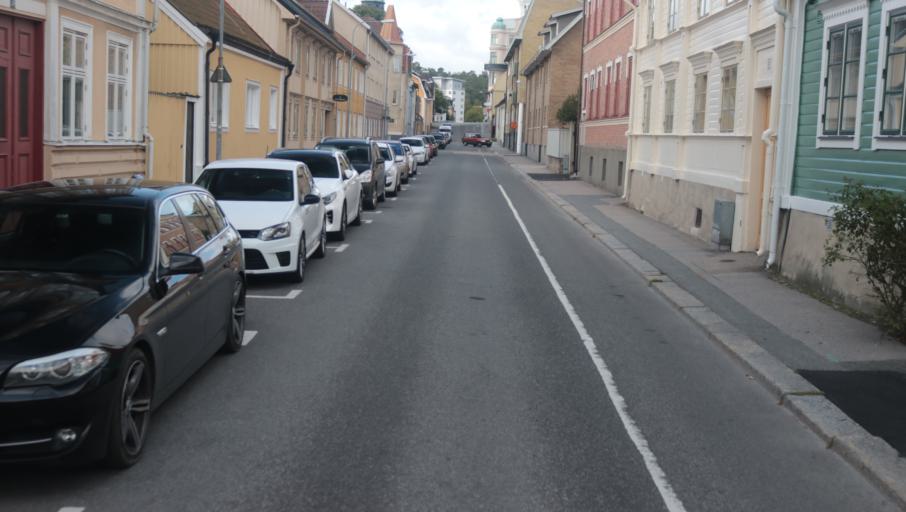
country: SE
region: Blekinge
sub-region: Karlshamns Kommun
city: Karlshamn
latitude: 56.1725
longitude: 14.8659
